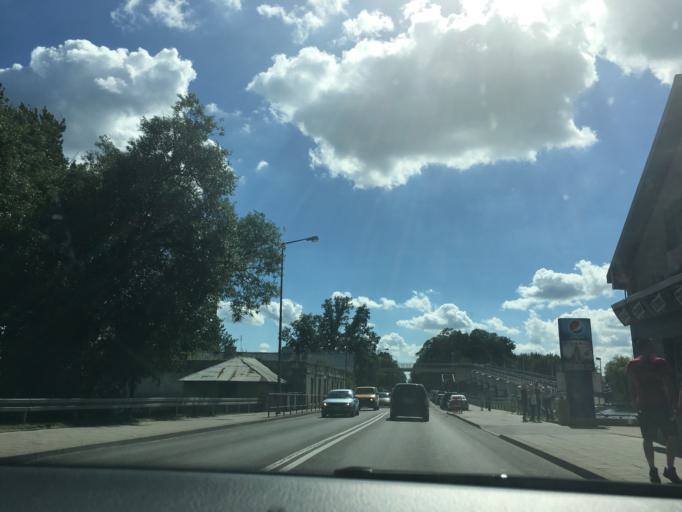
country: PL
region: Podlasie
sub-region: Powiat augustowski
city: Augustow
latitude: 53.8446
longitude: 22.9964
